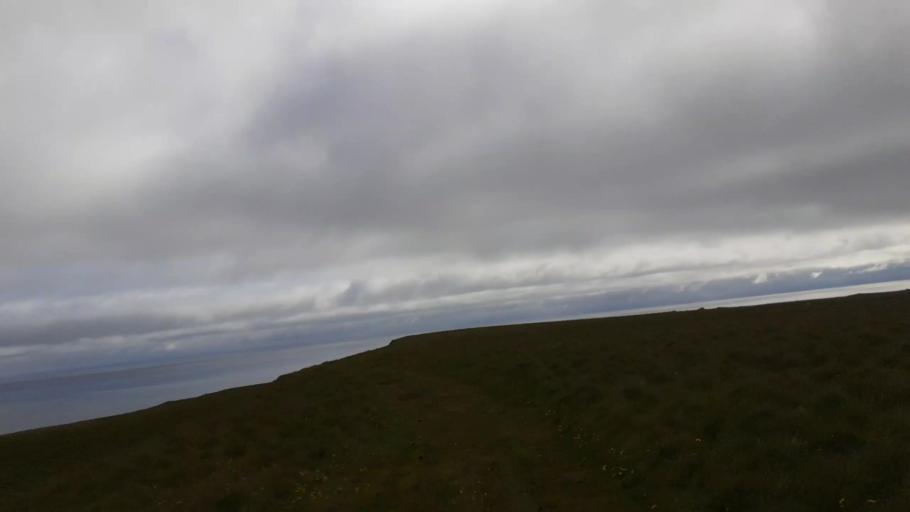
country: IS
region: Northeast
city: Dalvik
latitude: 66.5402
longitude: -17.9838
